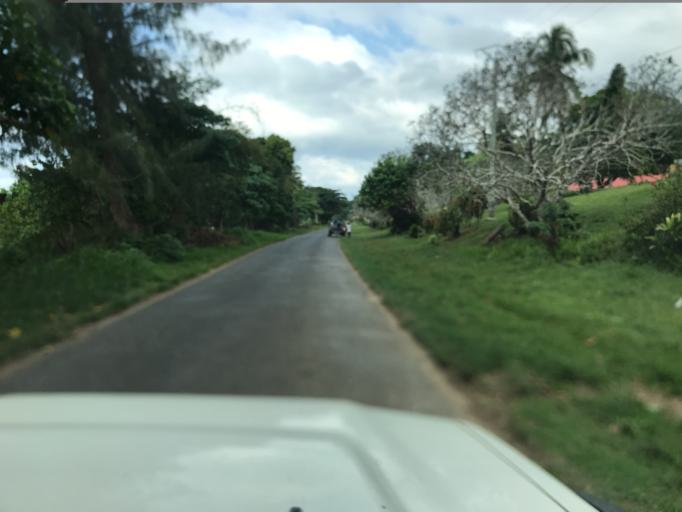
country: VU
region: Sanma
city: Luganville
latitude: -15.5430
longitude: 167.1499
